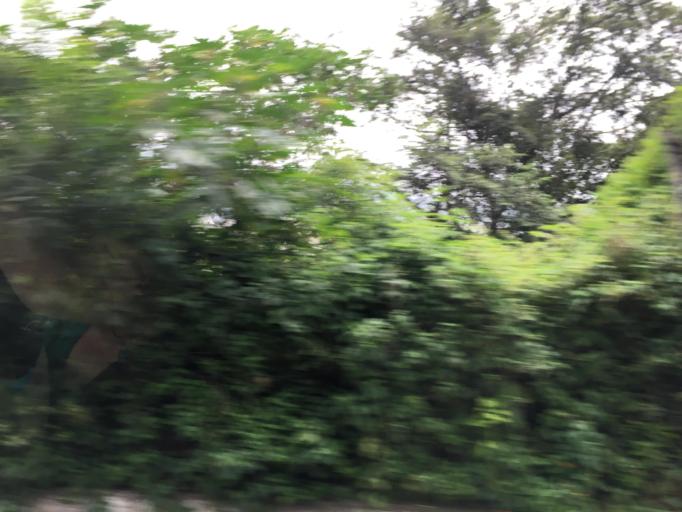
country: GT
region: Sacatepequez
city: Alotenango
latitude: 14.4824
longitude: -90.8081
